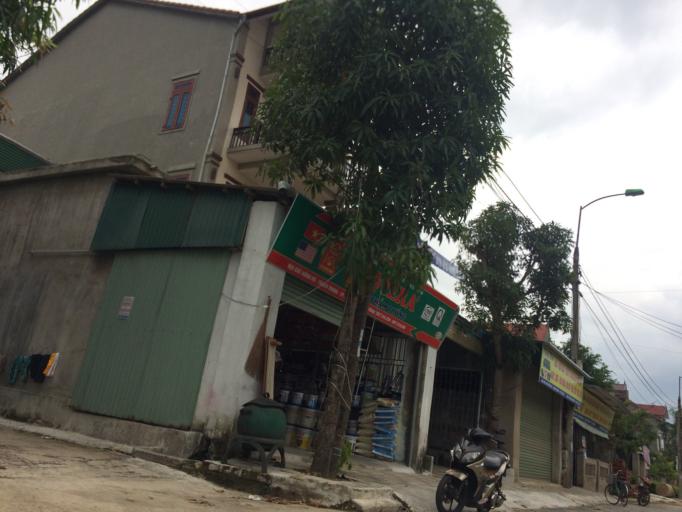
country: VN
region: Ha Tinh
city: Thach Ha
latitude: 18.3678
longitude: 105.8869
